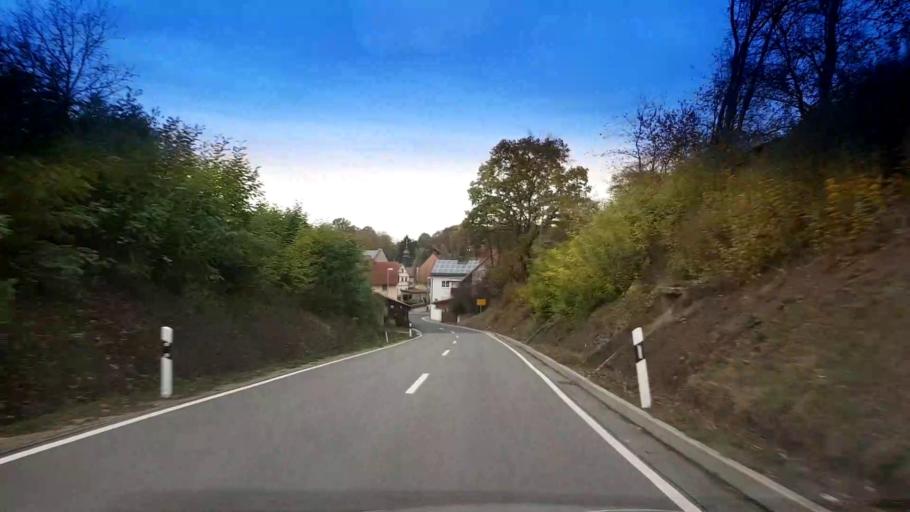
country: DE
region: Bavaria
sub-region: Upper Franconia
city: Priesendorf
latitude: 49.9293
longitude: 10.6968
